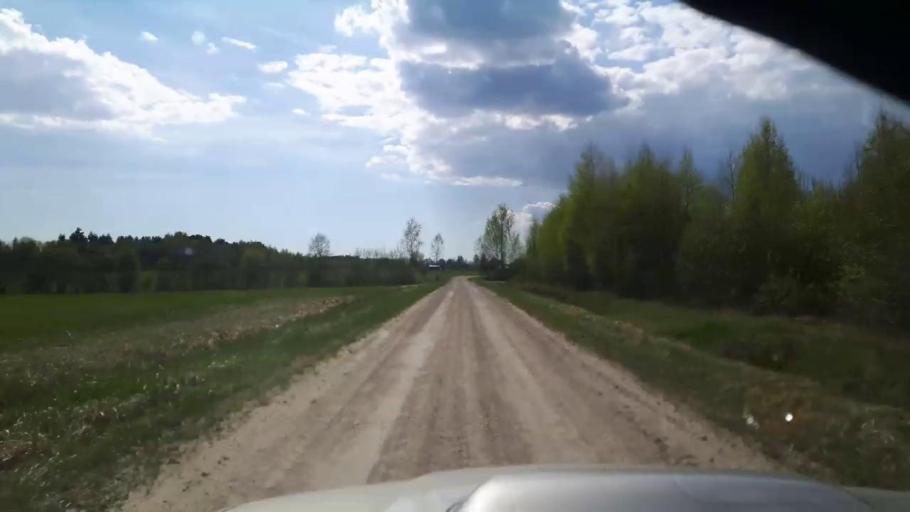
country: EE
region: Paernumaa
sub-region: Sindi linn
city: Sindi
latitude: 58.4261
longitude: 24.7603
